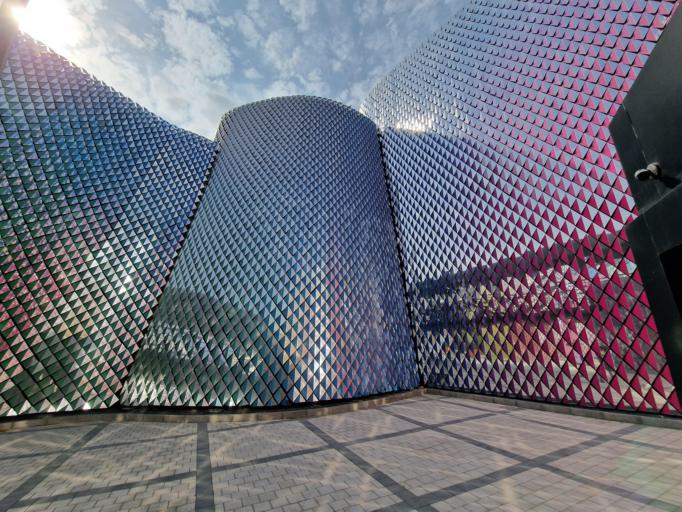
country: AE
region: Dubai
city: Dubai
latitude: 24.9657
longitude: 55.1513
